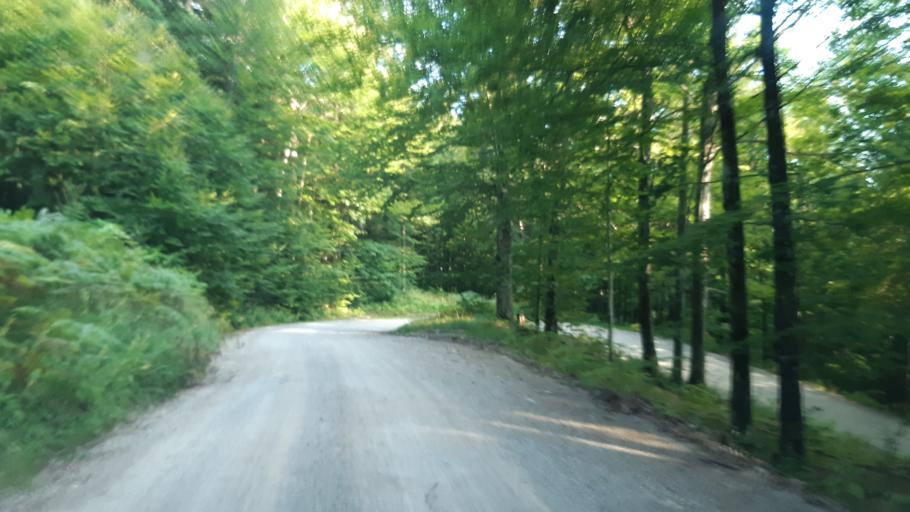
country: SI
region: Dolenjske Toplice
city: Dolenjske Toplice
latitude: 45.6720
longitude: 14.9881
